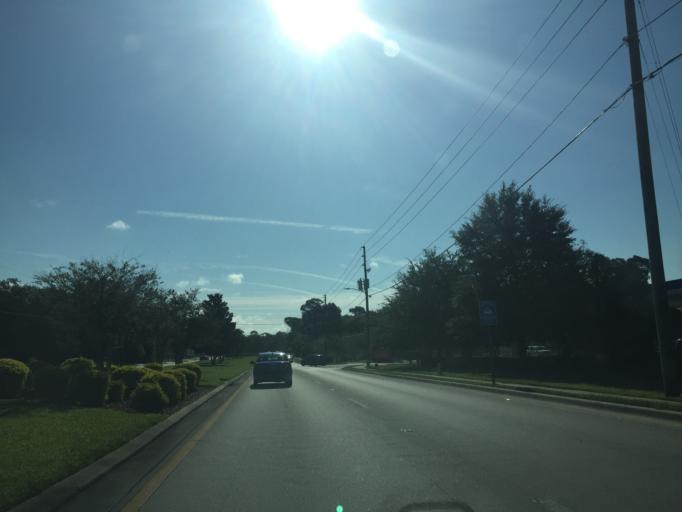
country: US
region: Florida
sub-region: Seminole County
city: Casselberry
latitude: 28.6750
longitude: -81.3175
